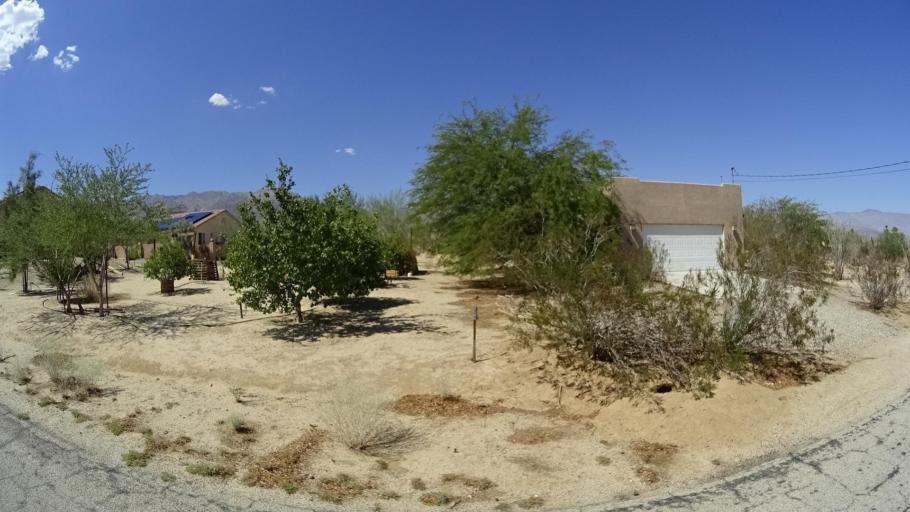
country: US
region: California
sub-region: San Diego County
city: Borrego Springs
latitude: 33.2182
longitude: -116.3714
